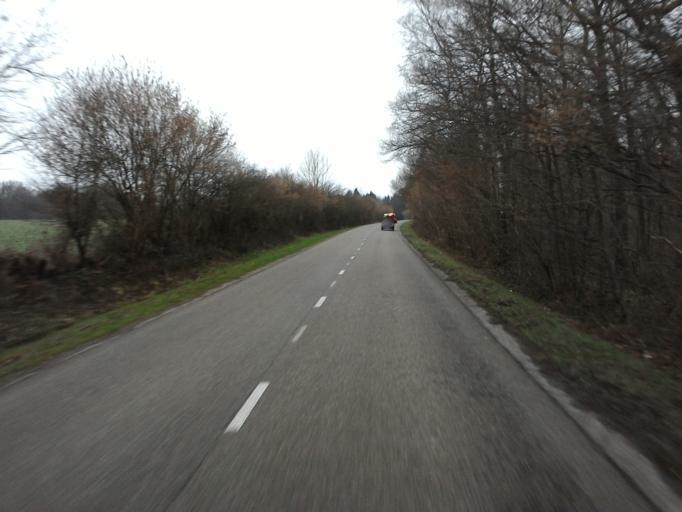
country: BE
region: Wallonia
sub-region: Province de Namur
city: Gedinne
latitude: 50.0387
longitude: 4.9595
